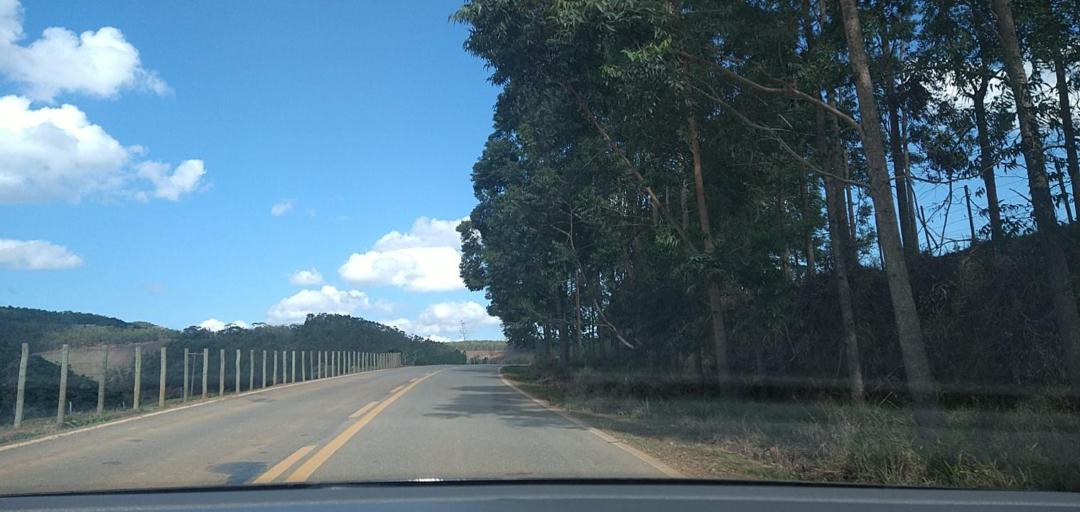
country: BR
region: Minas Gerais
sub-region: Alvinopolis
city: Alvinopolis
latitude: -20.0183
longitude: -43.0716
